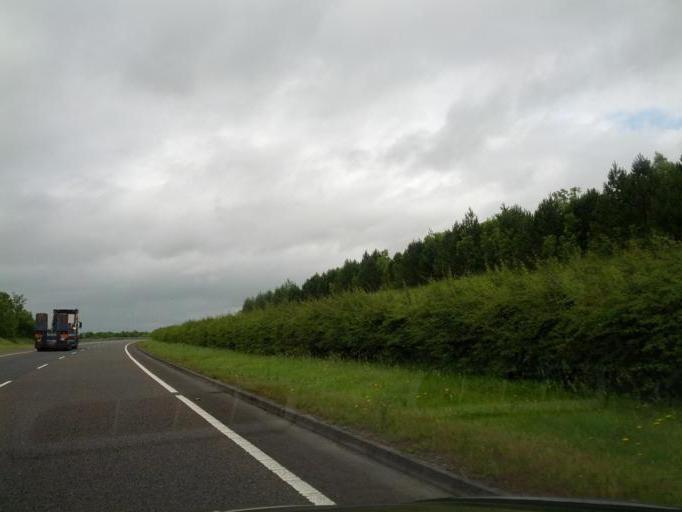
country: IE
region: Munster
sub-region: An Clar
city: Newmarket on Fergus
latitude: 52.7755
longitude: -8.9196
